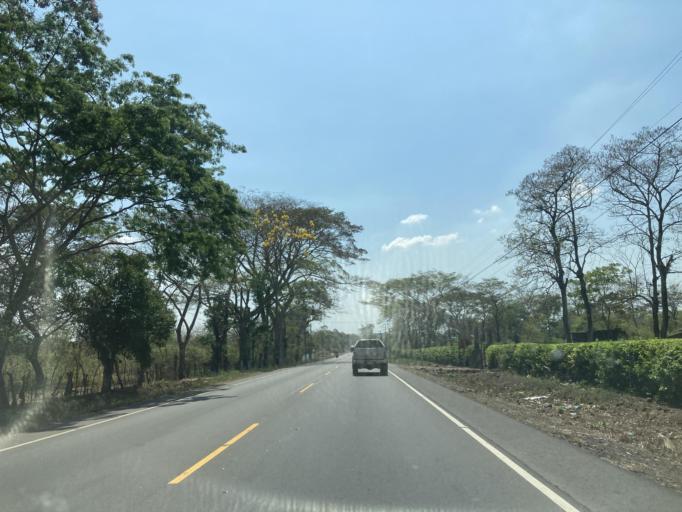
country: GT
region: Escuintla
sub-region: Municipio de Escuintla
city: Escuintla
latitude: 14.2342
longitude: -90.7399
